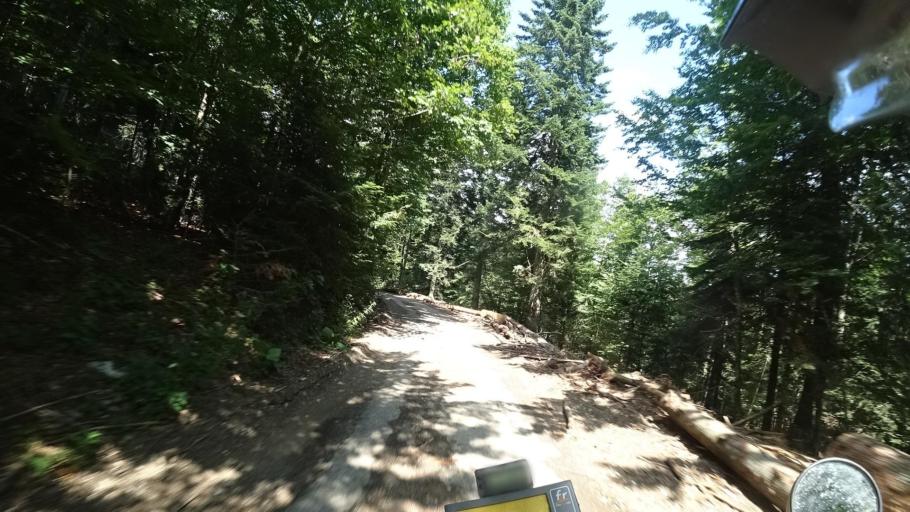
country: HR
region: Licko-Senjska
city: Brinje
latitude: 45.1030
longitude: 15.0205
